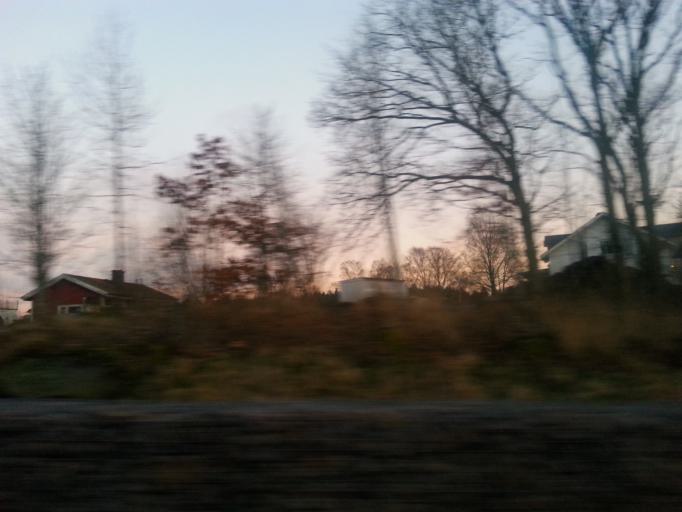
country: SE
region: Vaestra Goetaland
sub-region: Partille Kommun
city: Ojersjo
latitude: 57.6915
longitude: 12.1192
